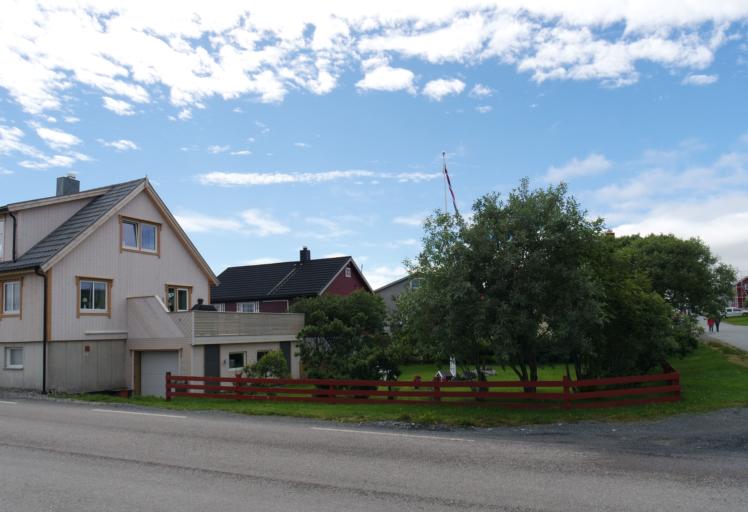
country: NO
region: Nordland
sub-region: Andoy
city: Andenes
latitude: 69.3205
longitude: 16.1259
